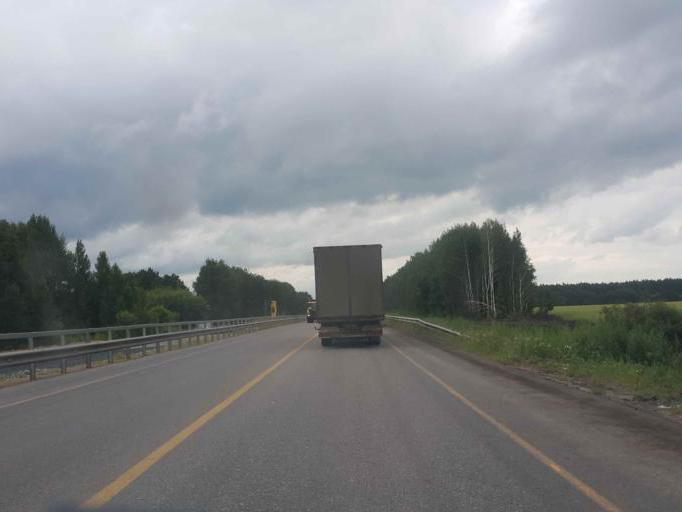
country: RU
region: Tambov
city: Selezni
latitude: 52.7999
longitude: 40.9863
